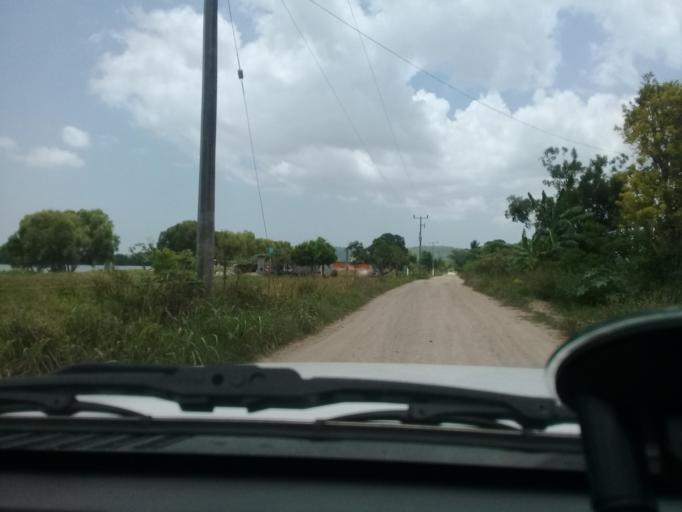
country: MX
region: Veracruz
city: Panuco
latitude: 22.1281
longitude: -98.0573
